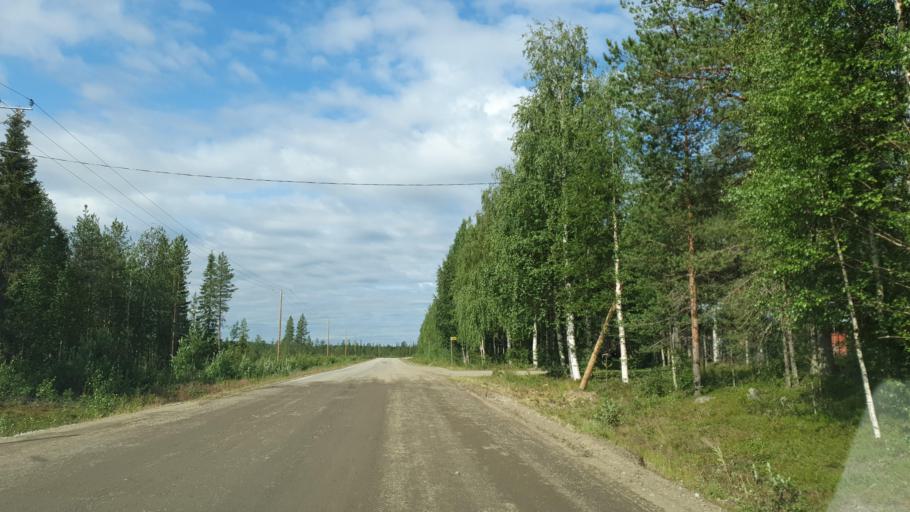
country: FI
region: Lapland
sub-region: Pohjois-Lappi
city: Sodankylae
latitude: 67.5258
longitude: 26.0015
